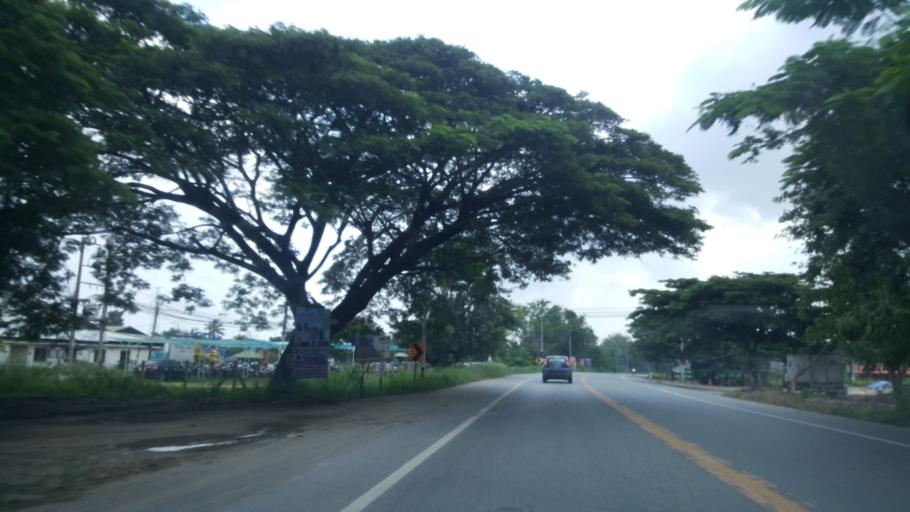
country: TH
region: Rayong
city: Ban Chang
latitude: 12.7274
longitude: 100.9772
